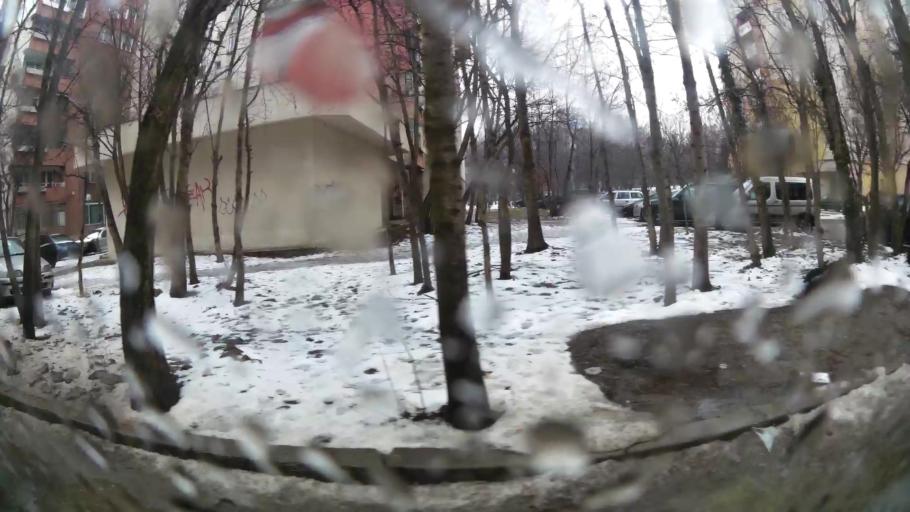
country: BG
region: Sofia-Capital
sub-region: Stolichna Obshtina
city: Sofia
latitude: 42.6742
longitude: 23.2943
